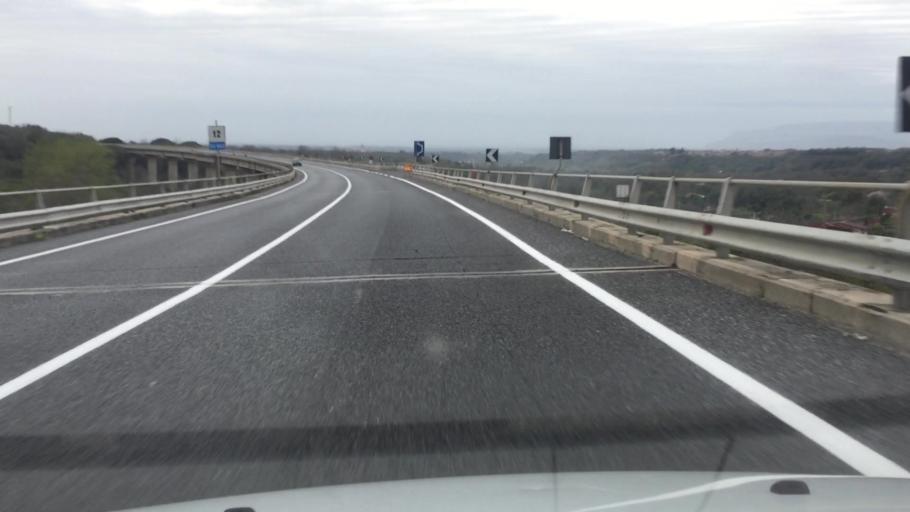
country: IT
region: Calabria
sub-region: Provincia di Reggio Calabria
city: Anoia Superiore
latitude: 38.4209
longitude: 16.0987
